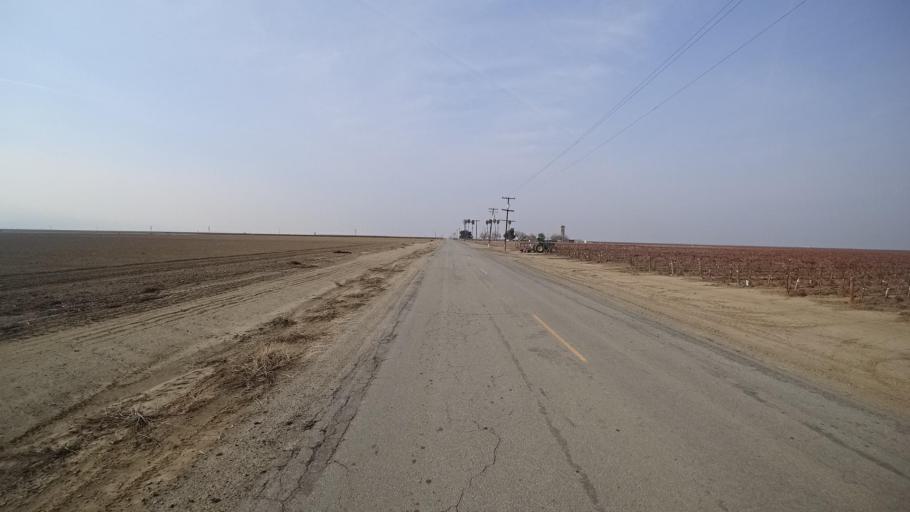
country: US
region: California
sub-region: Kern County
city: Greenfield
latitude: 35.0766
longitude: -119.0774
